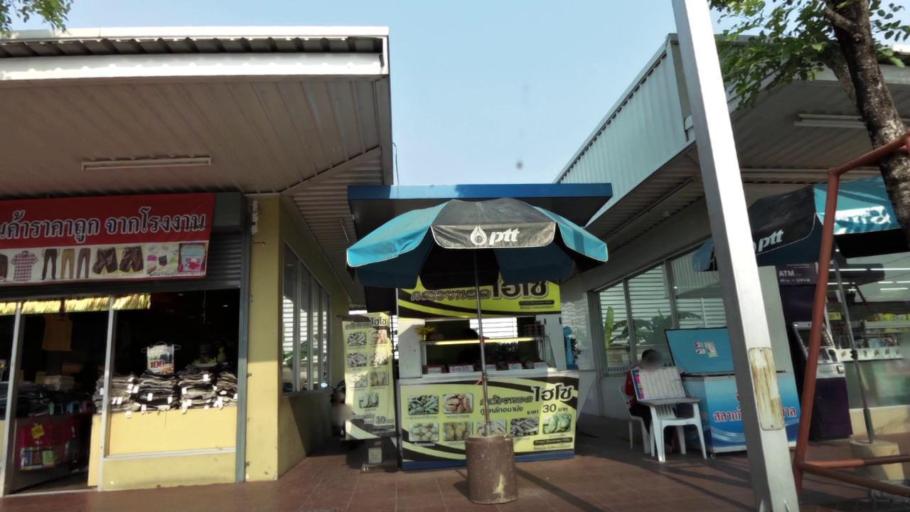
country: TH
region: Phra Nakhon Si Ayutthaya
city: Phra Nakhon Si Ayutthaya
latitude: 14.3288
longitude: 100.6240
